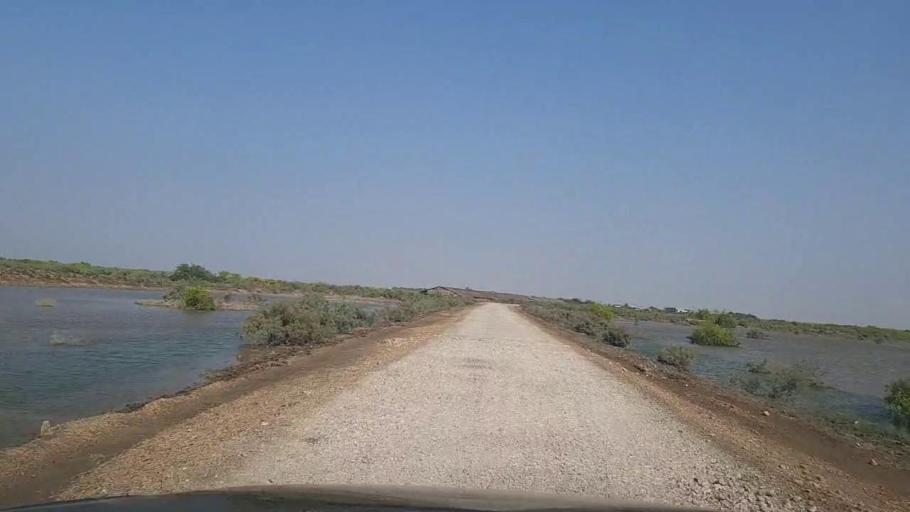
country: PK
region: Sindh
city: Thatta
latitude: 24.6434
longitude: 67.8156
